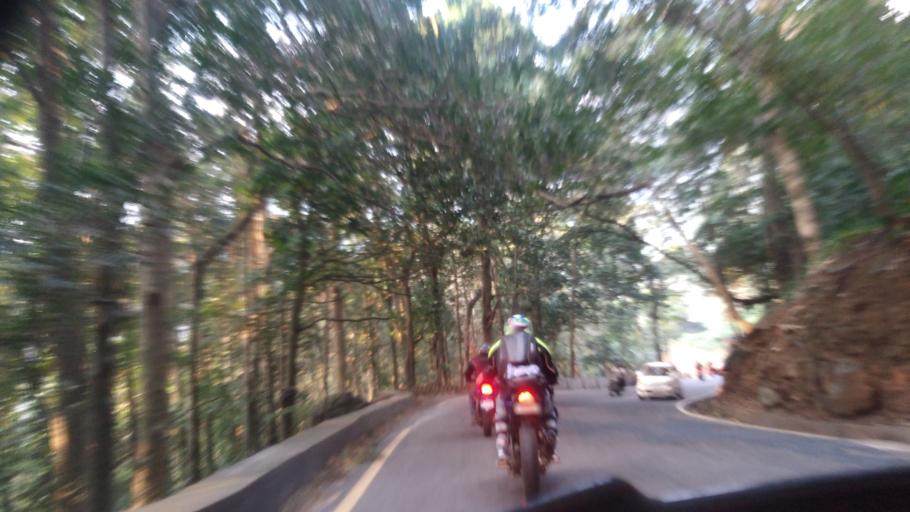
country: IN
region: Kerala
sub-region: Wayanad
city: Kalpetta
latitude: 11.5004
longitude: 76.0248
